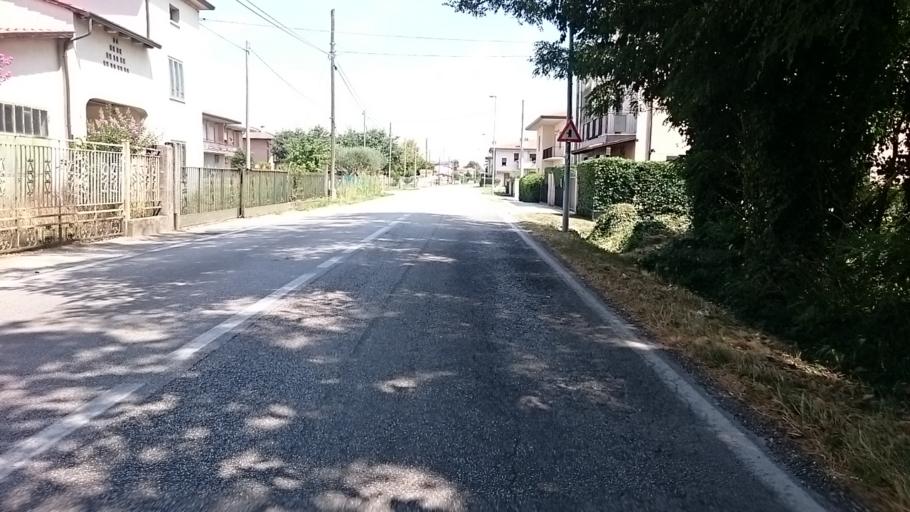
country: IT
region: Veneto
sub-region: Provincia di Vicenza
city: Rosa
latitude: 45.6930
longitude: 11.7412
